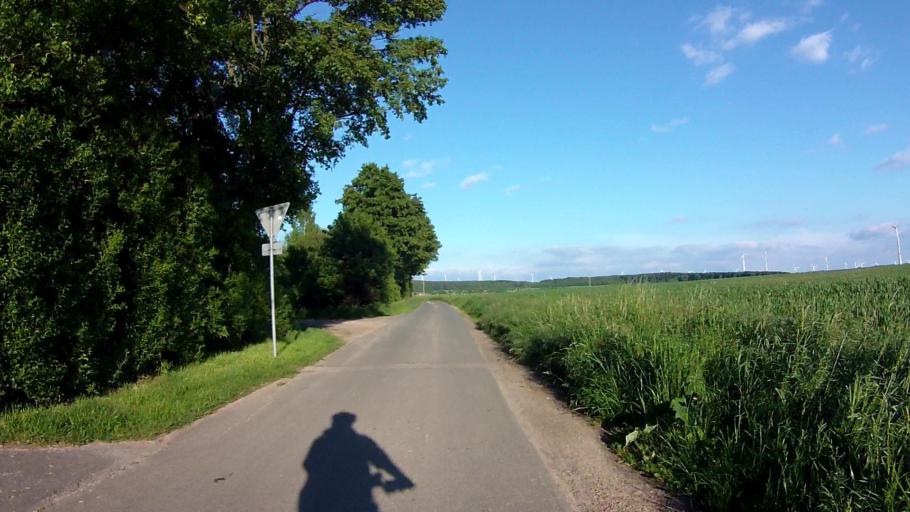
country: DE
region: North Rhine-Westphalia
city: Bad Lippspringe
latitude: 51.7420
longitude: 8.8418
